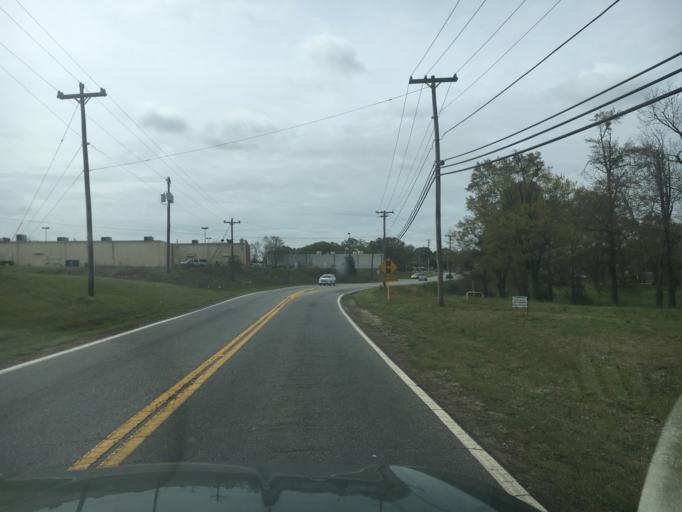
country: US
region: South Carolina
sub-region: Greenville County
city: Greer
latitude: 34.9501
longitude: -82.2128
